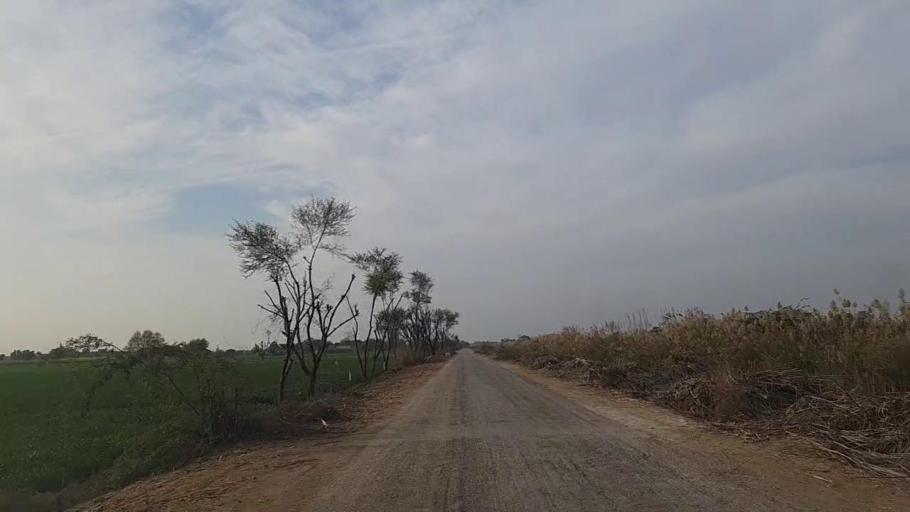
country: PK
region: Sindh
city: Daur
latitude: 26.4994
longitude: 68.4466
